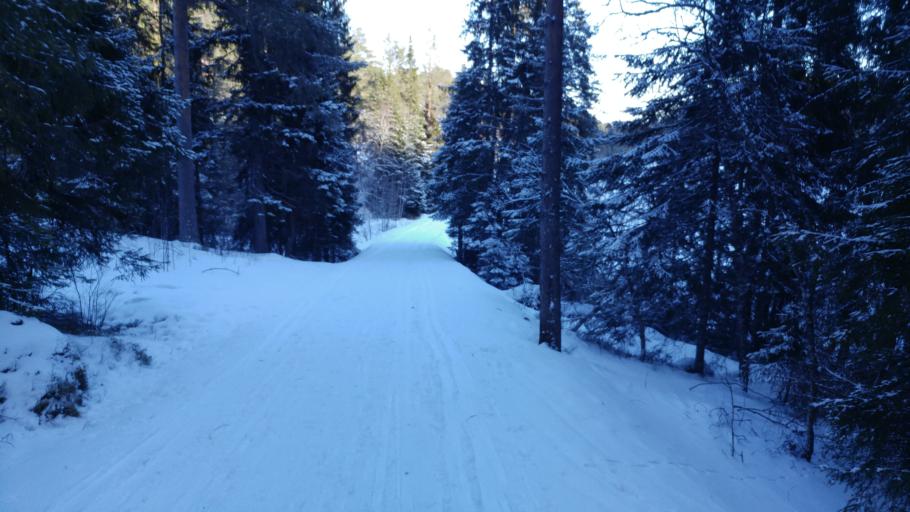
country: NO
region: Sor-Trondelag
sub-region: Trondheim
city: Trondheim
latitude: 63.4382
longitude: 10.3017
